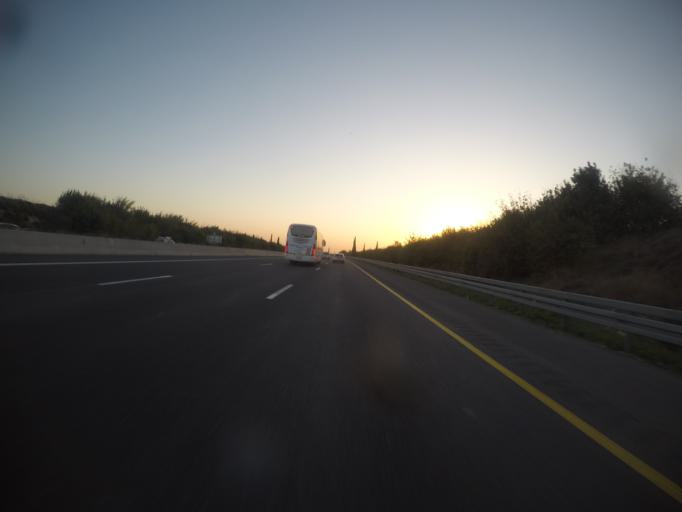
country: PS
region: West Bank
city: Nazlat `Isa
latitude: 32.4329
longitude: 35.0253
